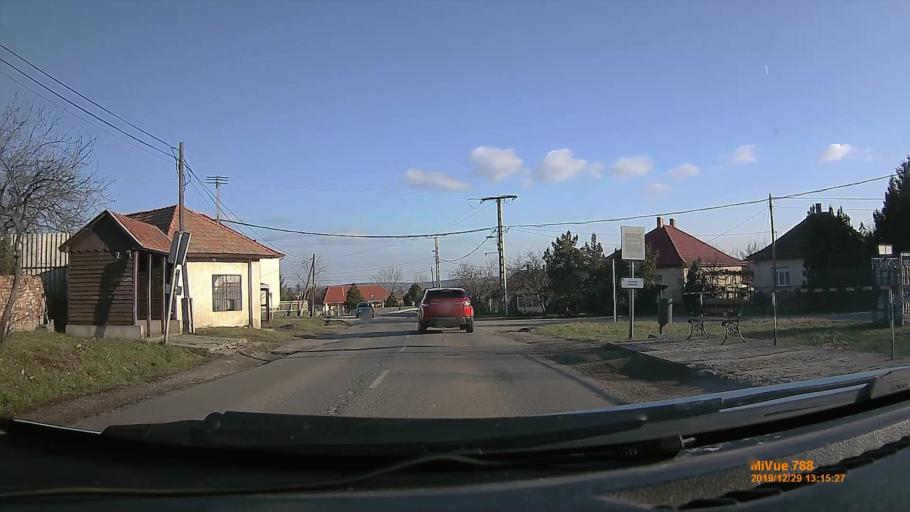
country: HU
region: Heves
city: Domoszlo
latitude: 47.8276
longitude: 20.1102
